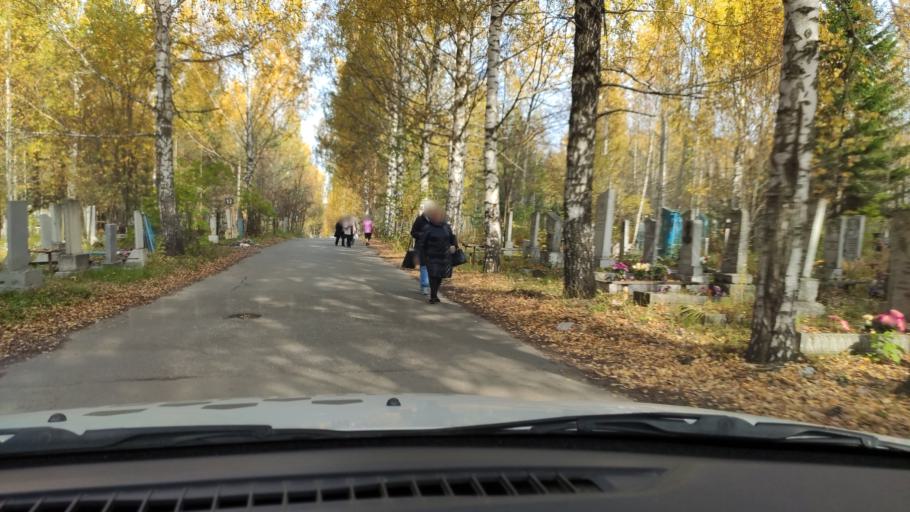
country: RU
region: Perm
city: Kondratovo
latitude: 58.0657
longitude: 56.1297
